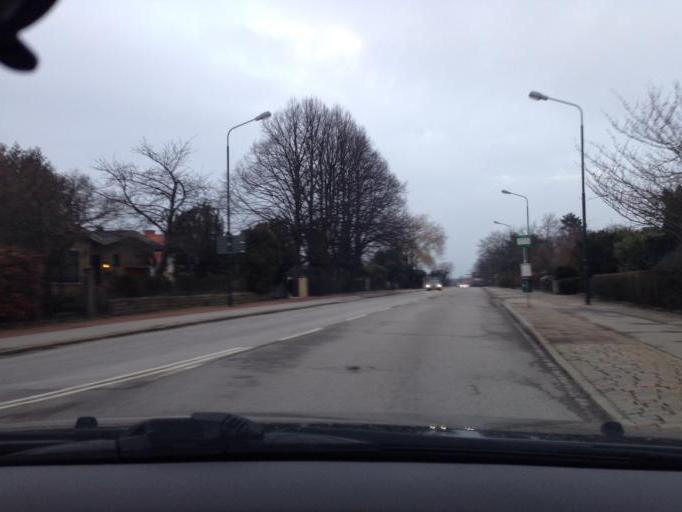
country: SE
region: Skane
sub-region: Malmo
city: Malmoe
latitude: 55.5822
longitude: 12.9669
